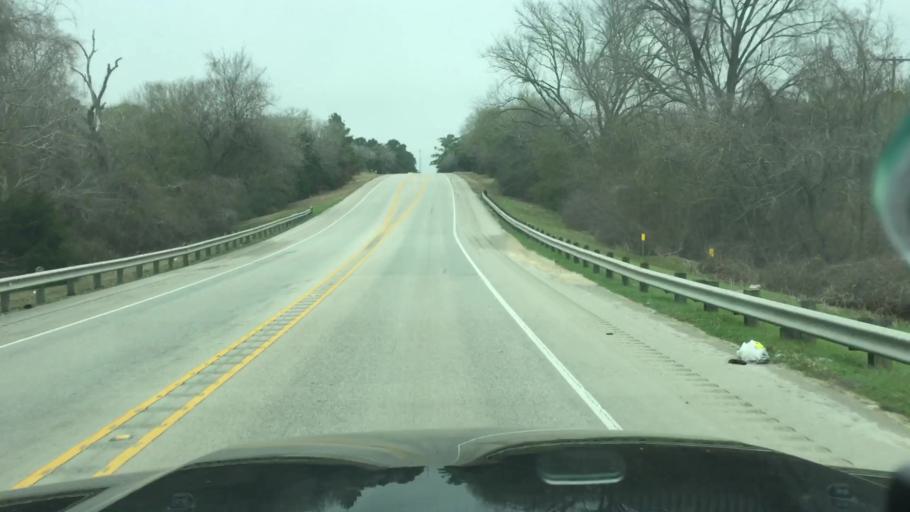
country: US
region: Texas
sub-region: Fayette County
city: La Grange
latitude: 30.0043
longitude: -96.8933
